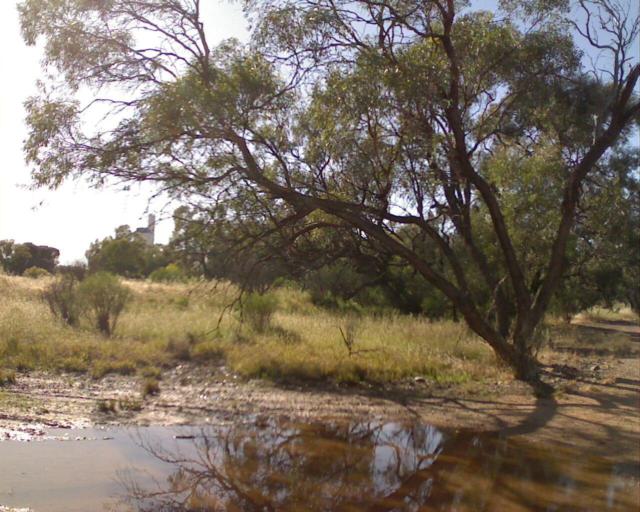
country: AU
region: South Australia
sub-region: Flinders Ranges
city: Quorn
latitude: -32.6502
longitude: 138.1046
